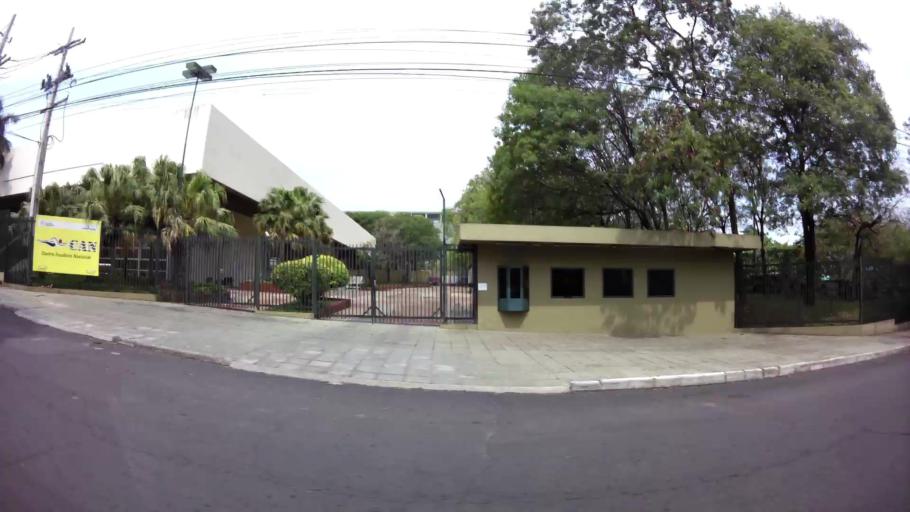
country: PY
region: Asuncion
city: Asuncion
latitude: -25.2766
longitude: -57.5776
